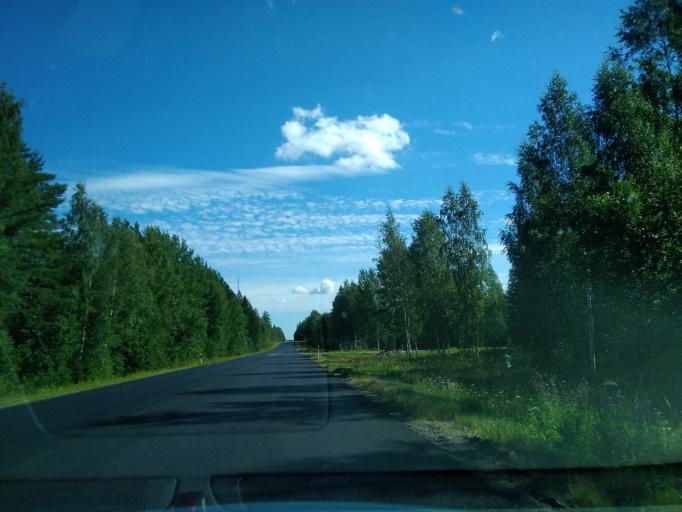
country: FI
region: Haeme
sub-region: Haemeenlinna
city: Renko
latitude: 60.9329
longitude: 24.3640
